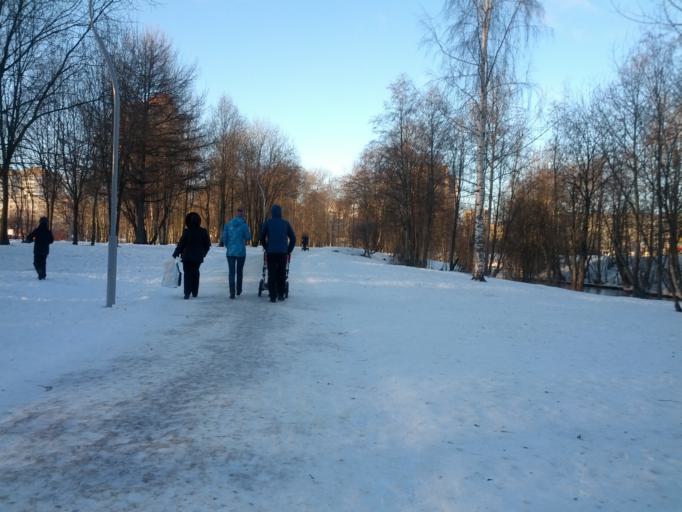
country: RU
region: St.-Petersburg
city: Krasnogvargeisky
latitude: 59.9118
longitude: 30.4853
